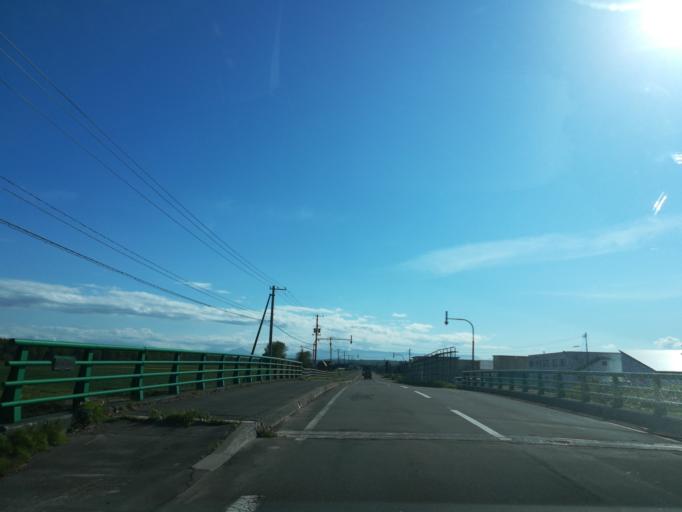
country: JP
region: Hokkaido
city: Kitahiroshima
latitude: 43.0464
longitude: 141.5957
